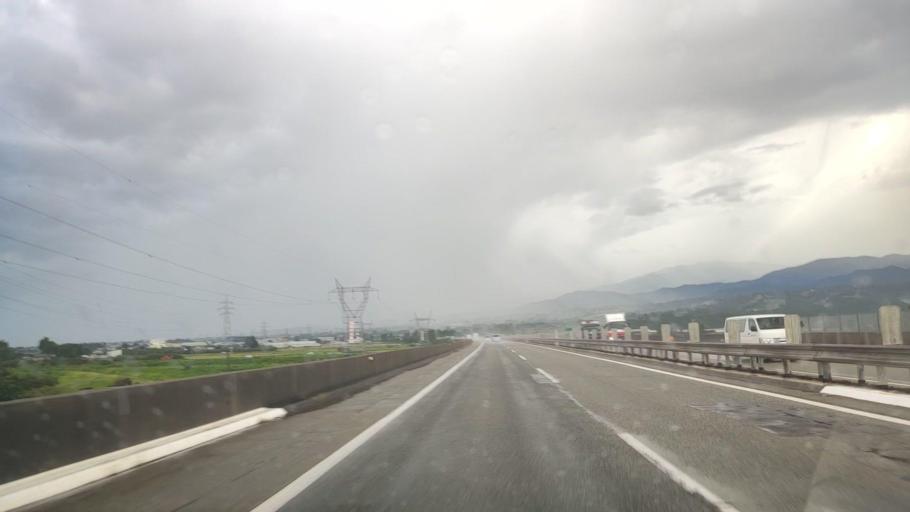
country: JP
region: Toyama
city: Kamiichi
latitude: 36.7246
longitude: 137.3609
